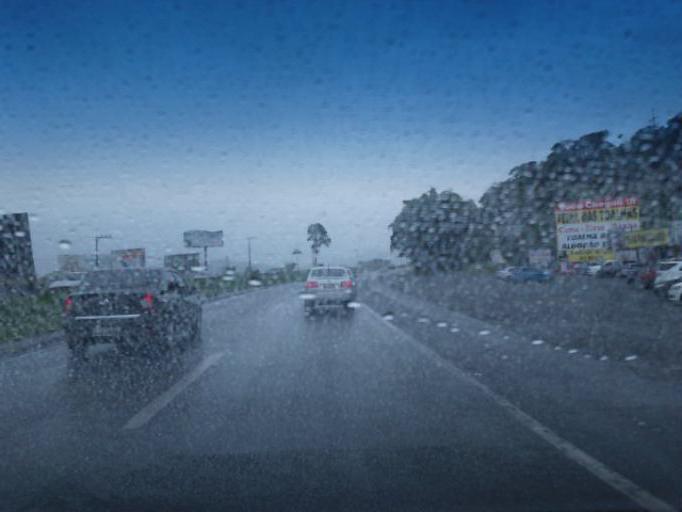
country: BR
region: Santa Catarina
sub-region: Navegantes
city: Navegantes
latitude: -26.8371
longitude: -48.7118
